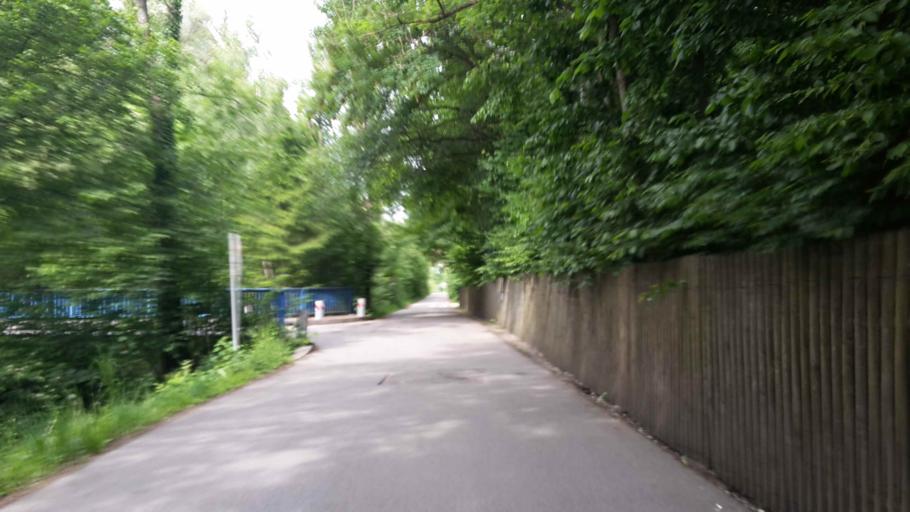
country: DE
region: Bavaria
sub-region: Upper Bavaria
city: Dachau
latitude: 48.2258
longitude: 11.4305
